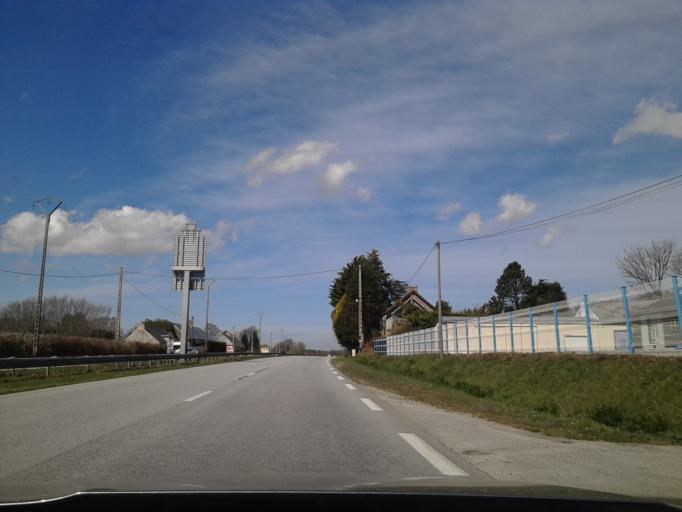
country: FR
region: Lower Normandy
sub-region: Departement de la Manche
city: Brix
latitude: 49.5701
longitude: -1.5748
